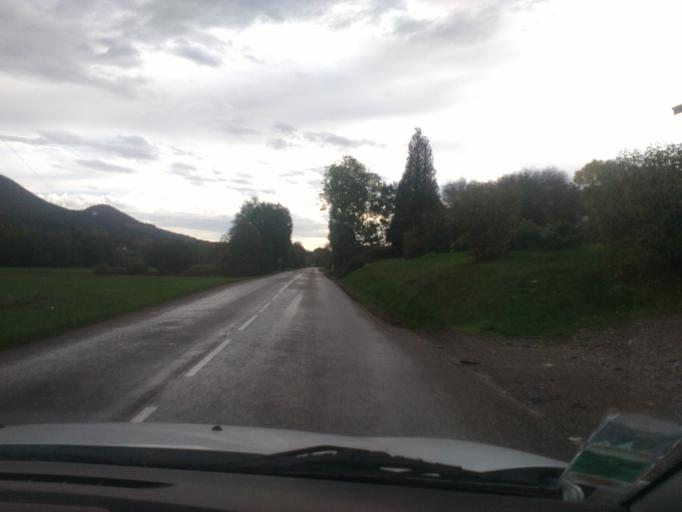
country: FR
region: Lorraine
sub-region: Departement des Vosges
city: Granges-sur-Vologne
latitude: 48.1823
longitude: 6.7997
